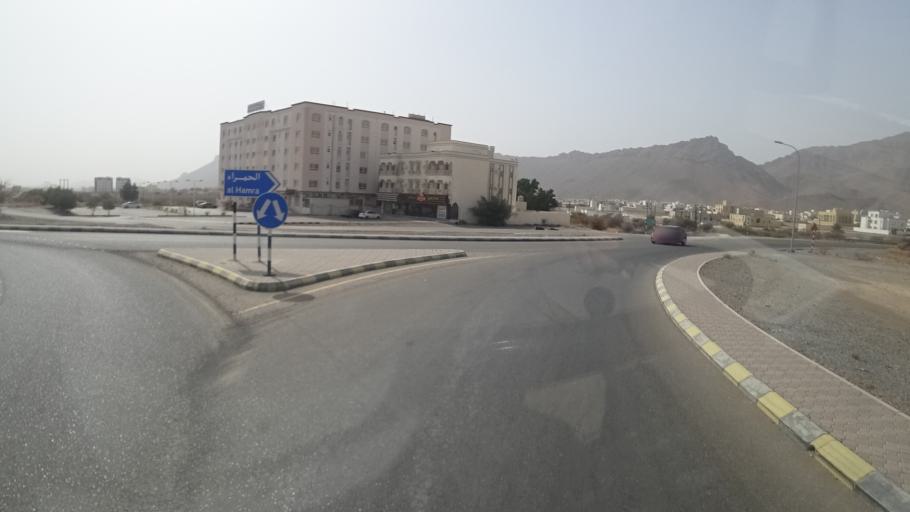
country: OM
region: Muhafazat ad Dakhiliyah
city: Nizwa
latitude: 22.9046
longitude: 57.5840
